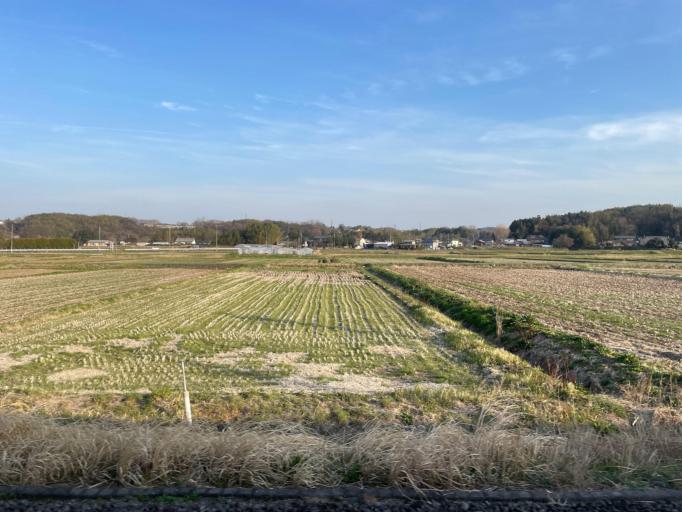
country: JP
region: Gunma
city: Annaka
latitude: 36.3132
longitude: 138.8840
